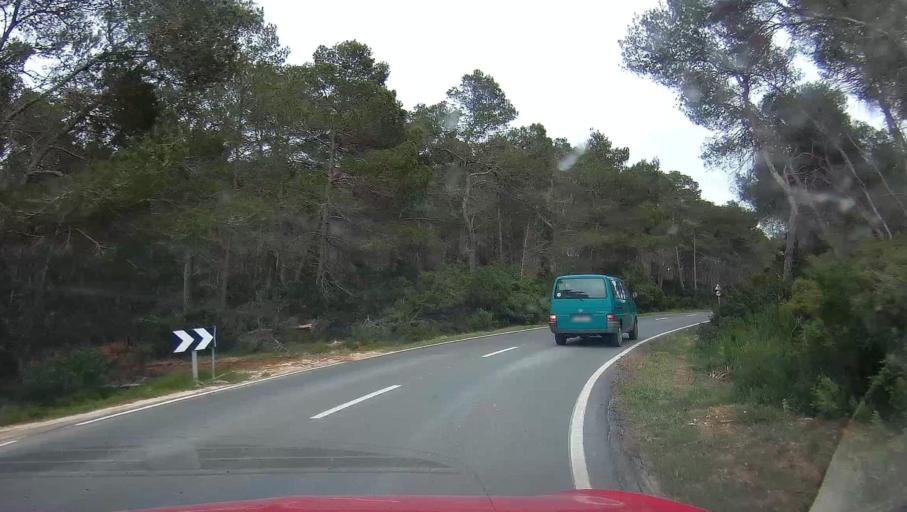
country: ES
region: Balearic Islands
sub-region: Illes Balears
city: Sant Joan de Labritja
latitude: 39.0481
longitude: 1.4087
